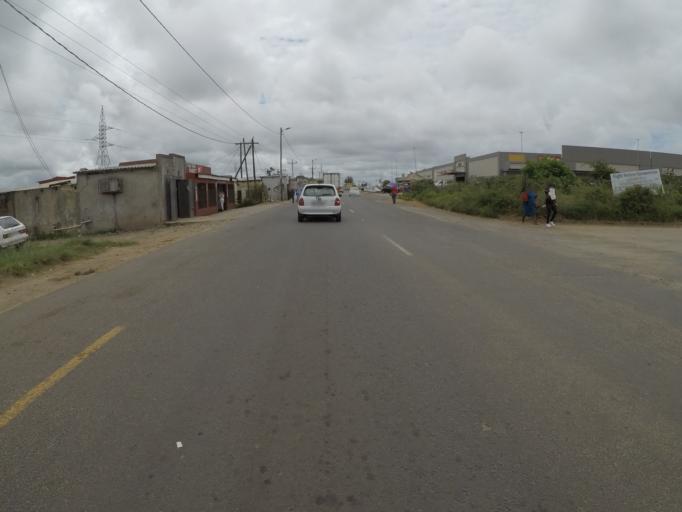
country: ZA
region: KwaZulu-Natal
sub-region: uThungulu District Municipality
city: eSikhawini
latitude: -28.8729
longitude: 31.8981
